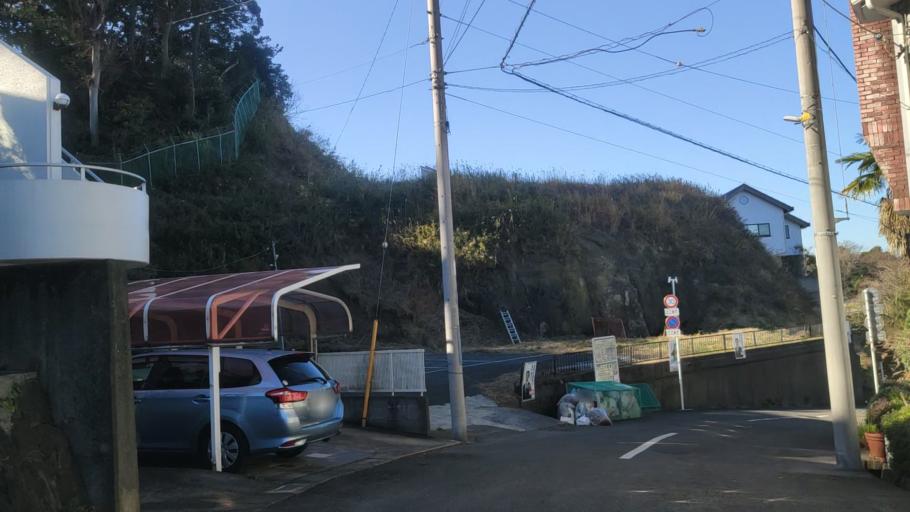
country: JP
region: Kanagawa
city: Yokohama
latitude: 35.4188
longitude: 139.6576
